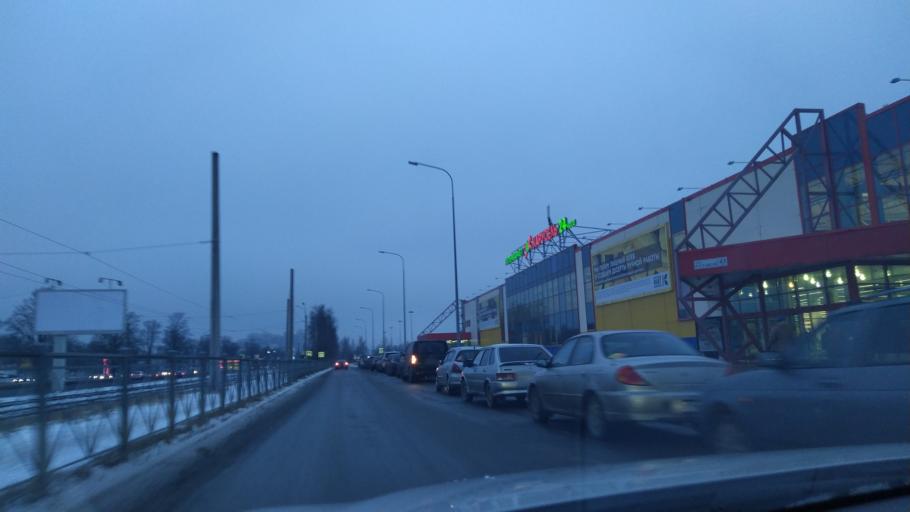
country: RU
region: St.-Petersburg
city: Grazhdanka
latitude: 60.0165
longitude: 30.4335
